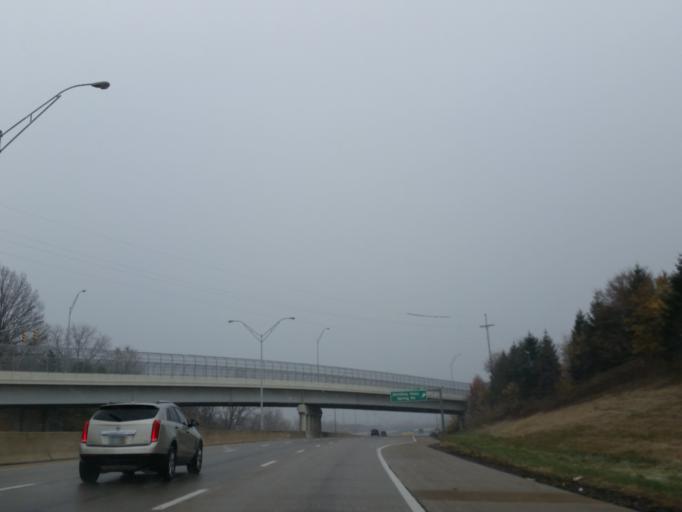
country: US
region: Ohio
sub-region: Cuyahoga County
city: Brooklyn Heights
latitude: 41.4398
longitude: -81.6837
